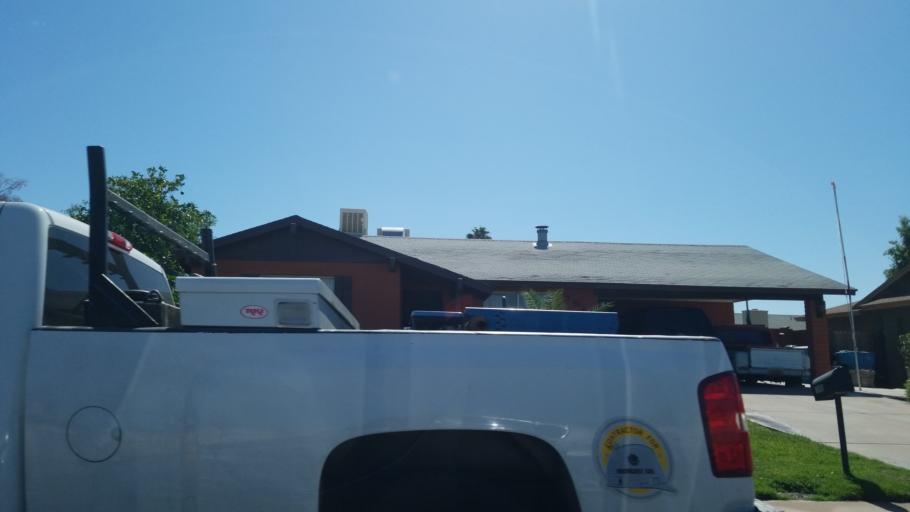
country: US
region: Arizona
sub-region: Maricopa County
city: Glendale
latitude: 33.5008
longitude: -112.2248
